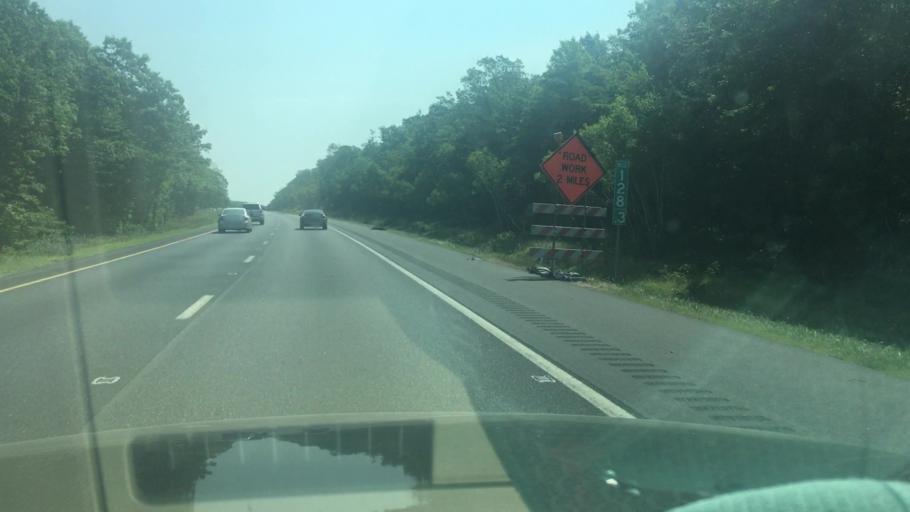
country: US
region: Pennsylvania
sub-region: Schuylkill County
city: Mahanoy City
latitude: 40.7880
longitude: -76.1459
